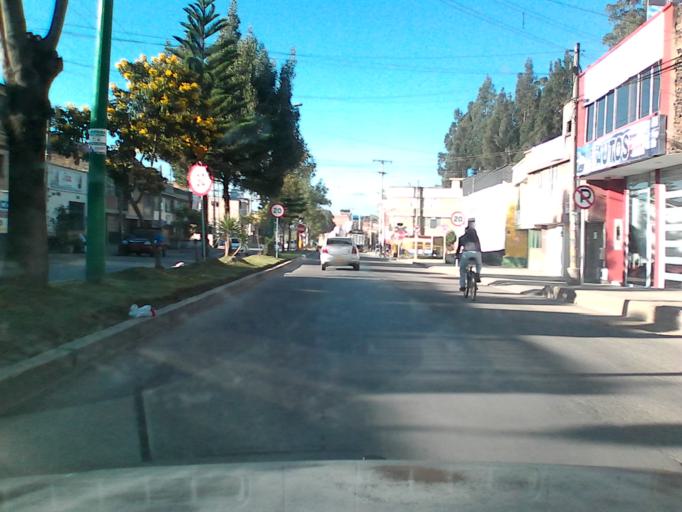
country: CO
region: Boyaca
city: Duitama
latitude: 5.8235
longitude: -73.0273
